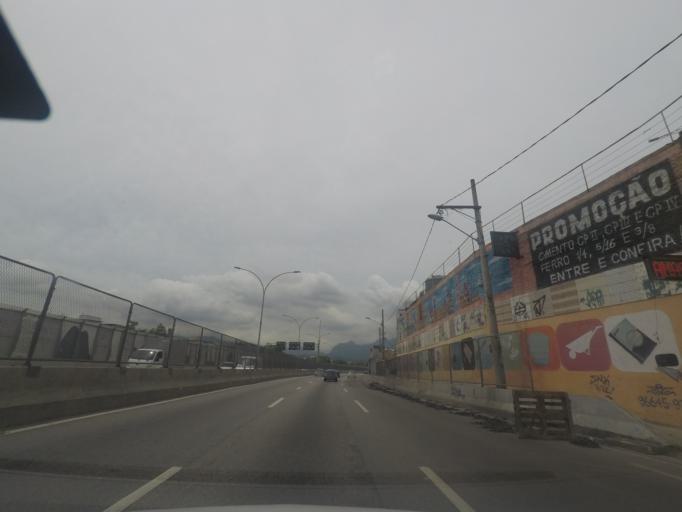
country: BR
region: Rio de Janeiro
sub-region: Rio De Janeiro
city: Rio de Janeiro
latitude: -22.8655
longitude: -43.2398
